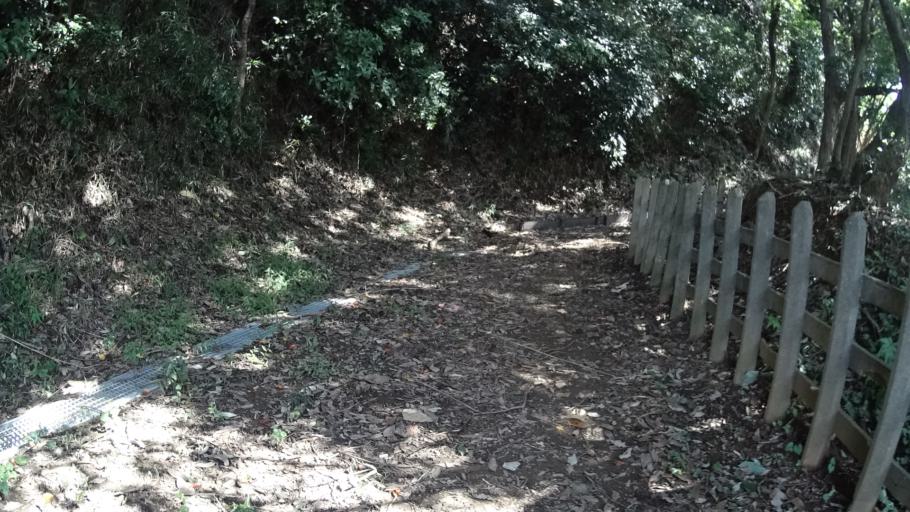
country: JP
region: Kanagawa
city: Kamakura
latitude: 35.3570
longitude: 139.5848
